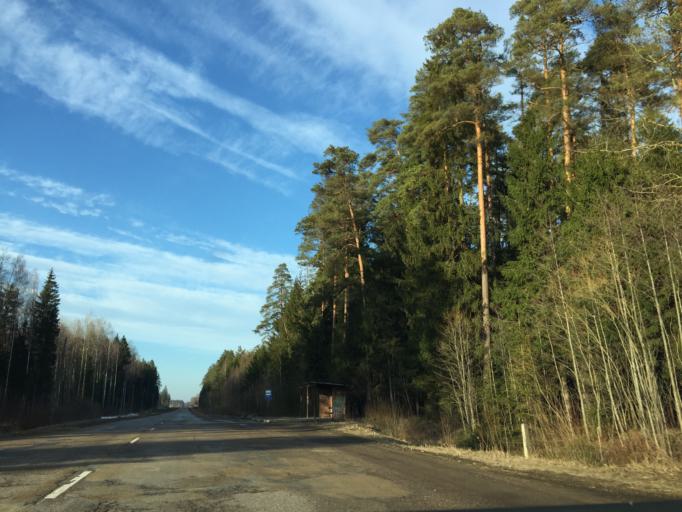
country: LV
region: Lecava
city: Iecava
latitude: 56.7195
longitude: 24.1114
